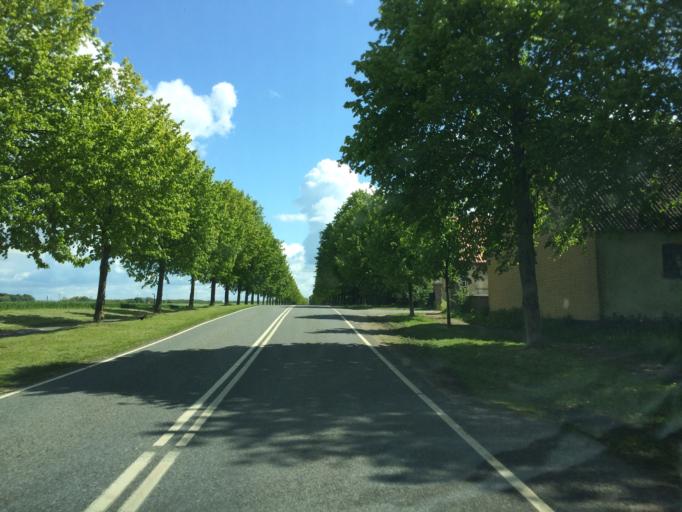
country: DK
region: Zealand
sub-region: Lejre Kommune
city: Lejre
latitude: 55.6124
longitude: 11.9829
